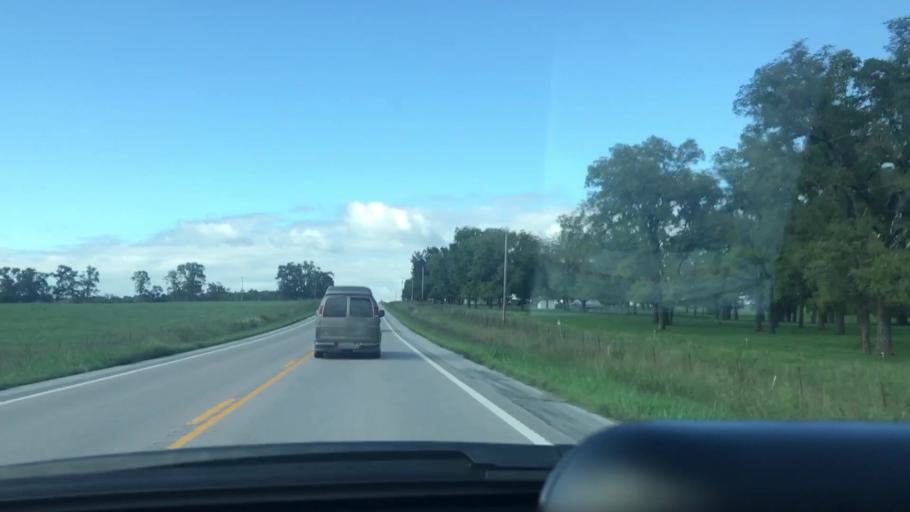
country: US
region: Missouri
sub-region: Hickory County
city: Hermitage
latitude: 37.9710
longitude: -93.2063
